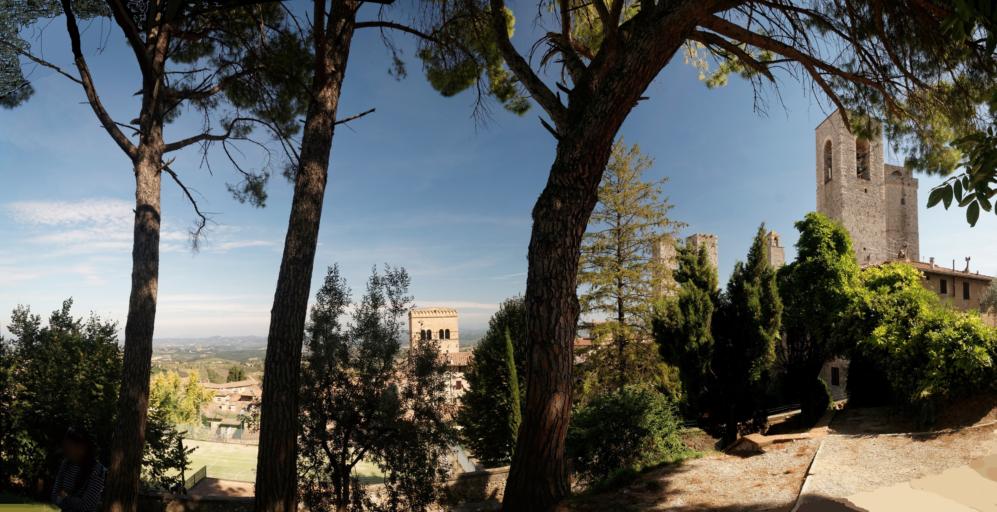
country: IT
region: Tuscany
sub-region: Provincia di Siena
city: San Gimignano
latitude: 43.4682
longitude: 11.0418
